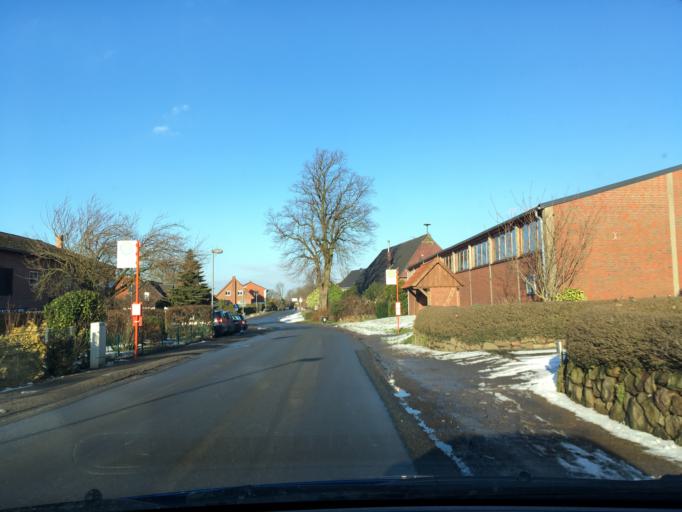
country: DE
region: Schleswig-Holstein
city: Schulendorf
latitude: 53.4713
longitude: 10.5678
